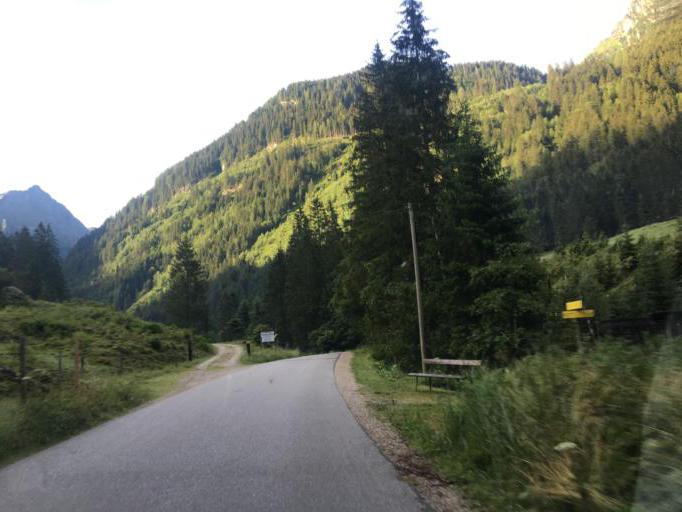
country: AT
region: Styria
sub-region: Politischer Bezirk Liezen
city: Haus
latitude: 47.3312
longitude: 13.7541
